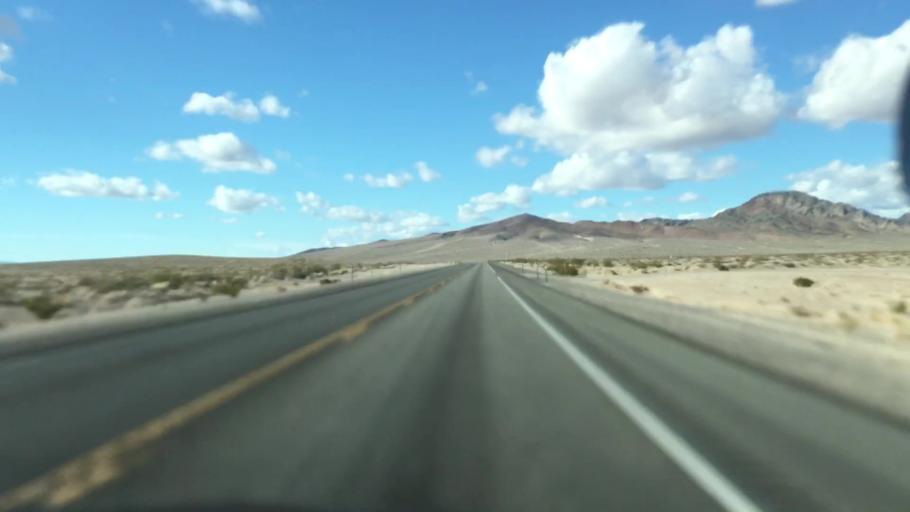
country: US
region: Nevada
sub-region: Nye County
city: Beatty
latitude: 36.6266
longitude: -116.3103
